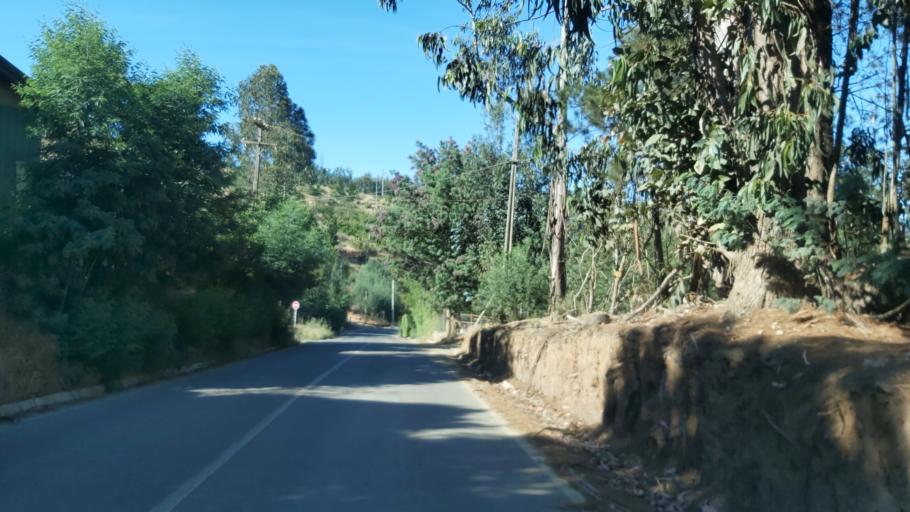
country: CL
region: Maule
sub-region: Provincia de Talca
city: Constitucion
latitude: -34.8444
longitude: -72.0521
